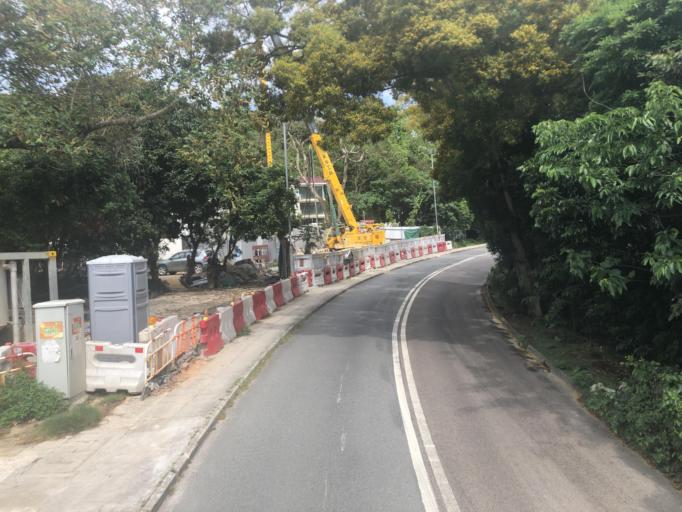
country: HK
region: Sai Kung
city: Sai Kung
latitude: 22.3965
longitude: 114.2859
